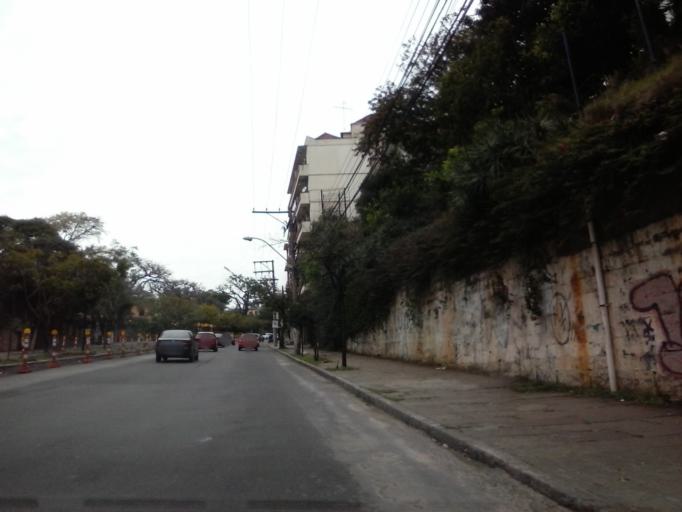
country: BR
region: Rio Grande do Sul
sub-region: Porto Alegre
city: Porto Alegre
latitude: -30.0406
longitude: -51.1946
